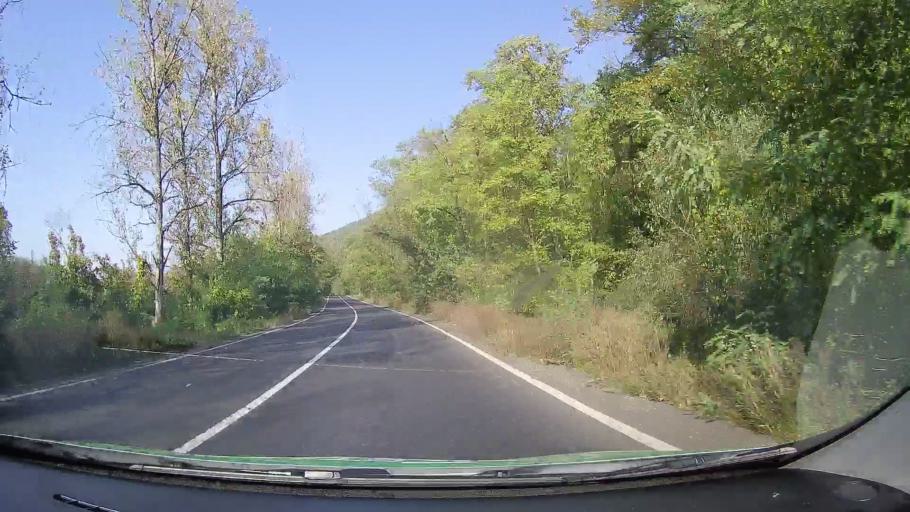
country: RO
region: Arad
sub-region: Comuna Savarsin
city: Savarsin
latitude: 46.0077
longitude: 22.2736
